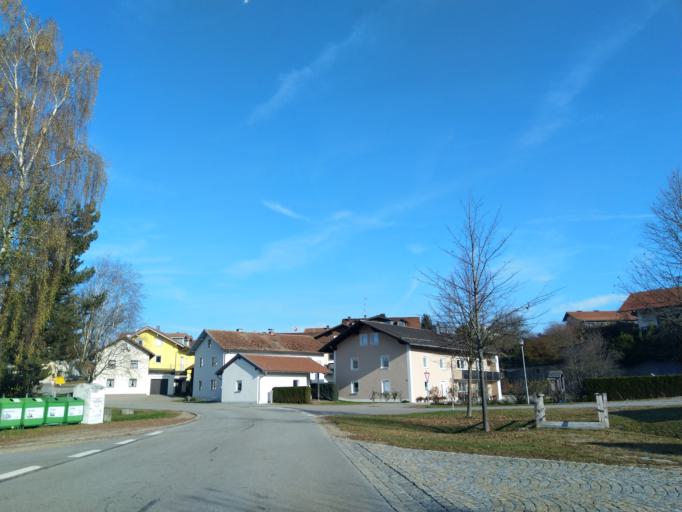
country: DE
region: Bavaria
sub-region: Lower Bavaria
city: Kirchberg
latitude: 48.9044
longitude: 13.1381
